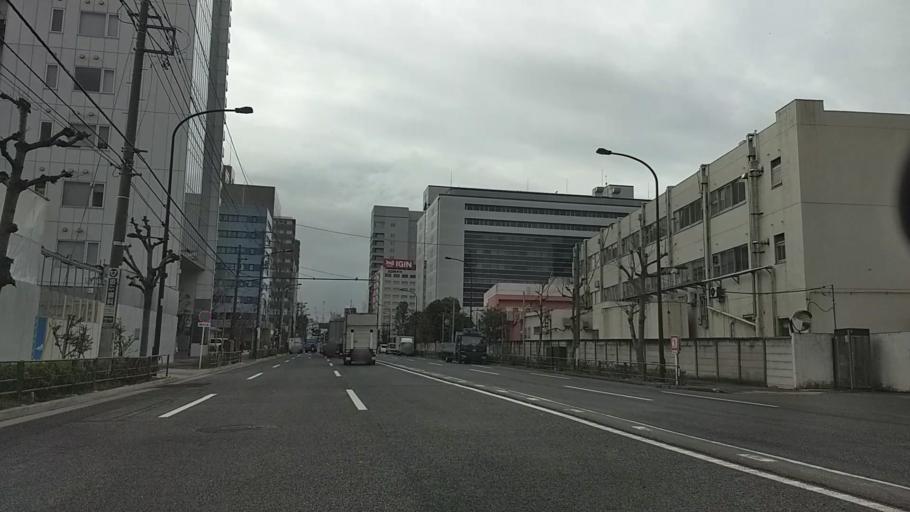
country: JP
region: Tokyo
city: Tokyo
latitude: 35.6270
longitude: 139.7447
